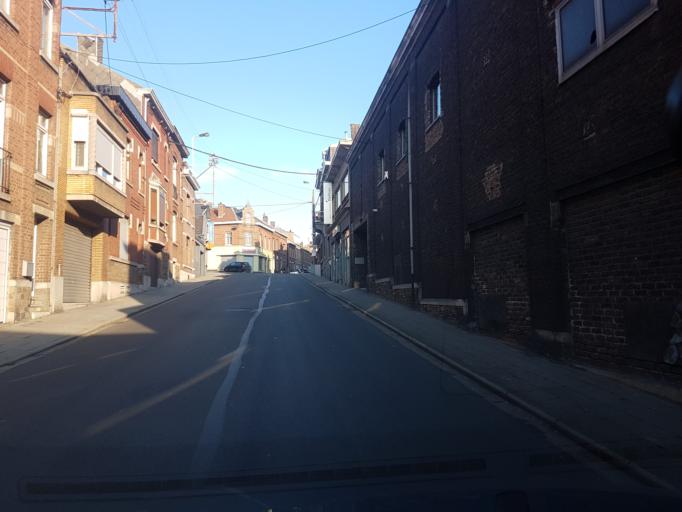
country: BE
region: Wallonia
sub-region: Province de Liege
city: Chaudfontaine
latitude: 50.6139
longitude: 5.6155
